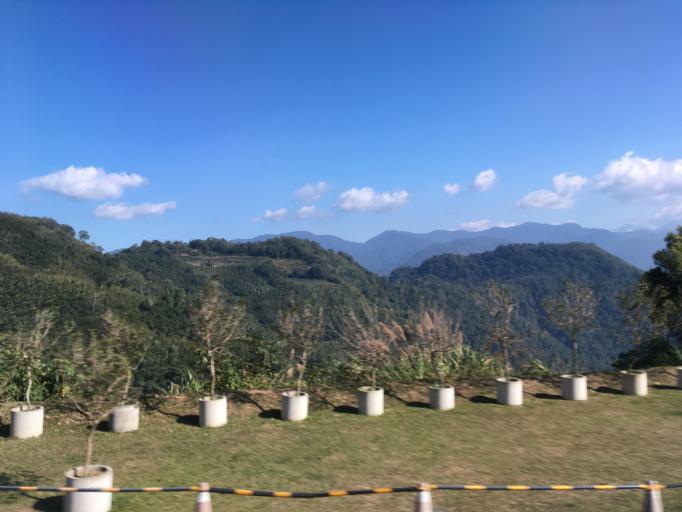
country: TW
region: Taiwan
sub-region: Chiayi
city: Jiayi Shi
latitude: 23.4070
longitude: 120.6544
